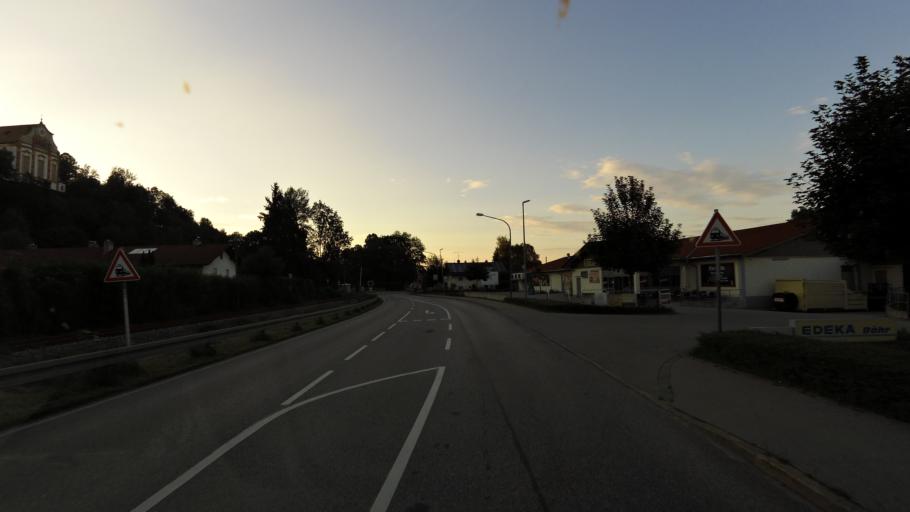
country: DE
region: Bavaria
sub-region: Upper Bavaria
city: Trostberg an der Alz
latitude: 47.9974
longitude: 12.5348
